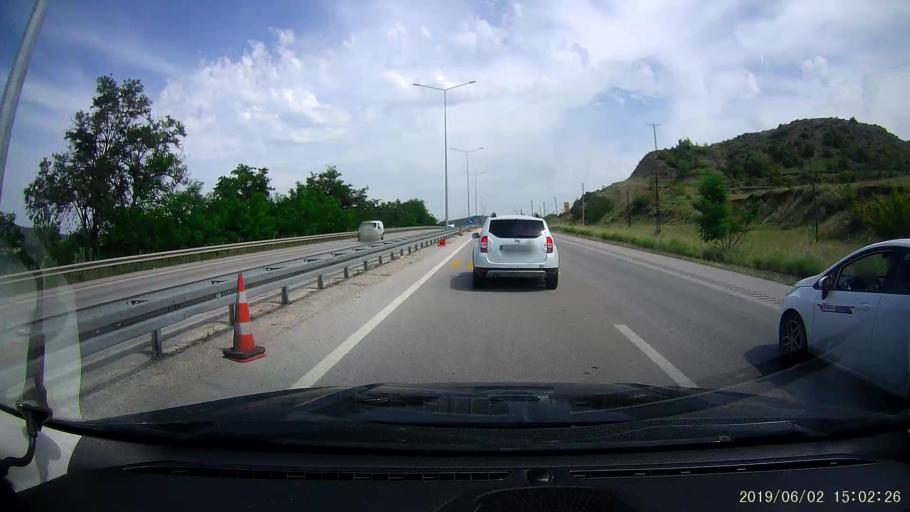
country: TR
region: Corum
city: Osmancik
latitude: 40.9809
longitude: 34.7671
